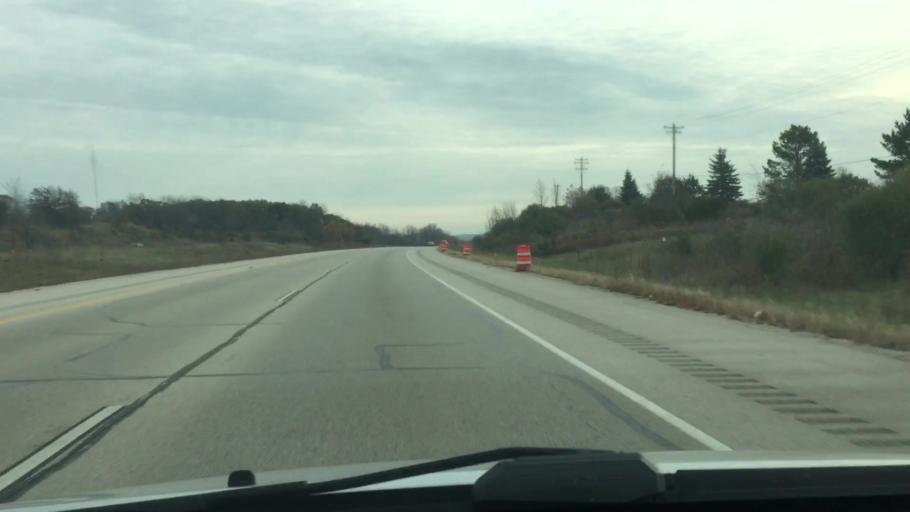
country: US
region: Wisconsin
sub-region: Waukesha County
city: Muskego
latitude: 42.9274
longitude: -88.1831
